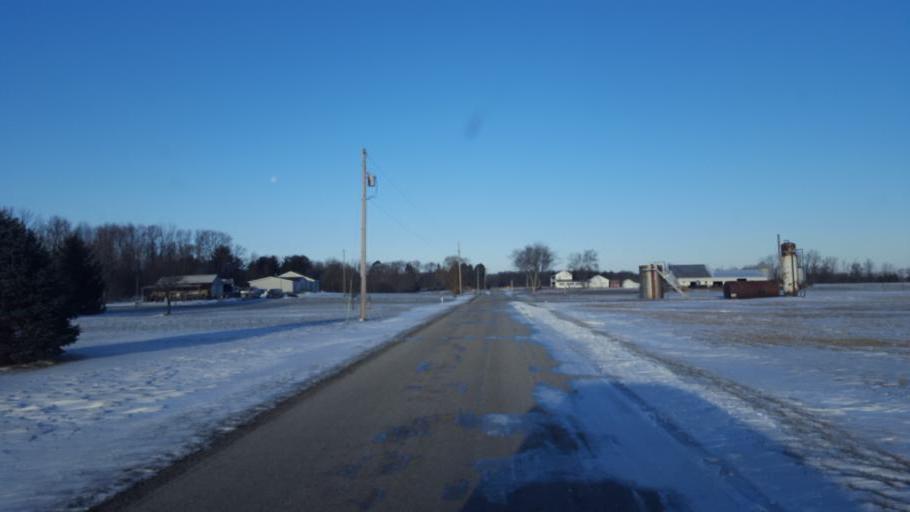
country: US
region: Ohio
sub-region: Morrow County
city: Cardington
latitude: 40.5164
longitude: -82.8950
